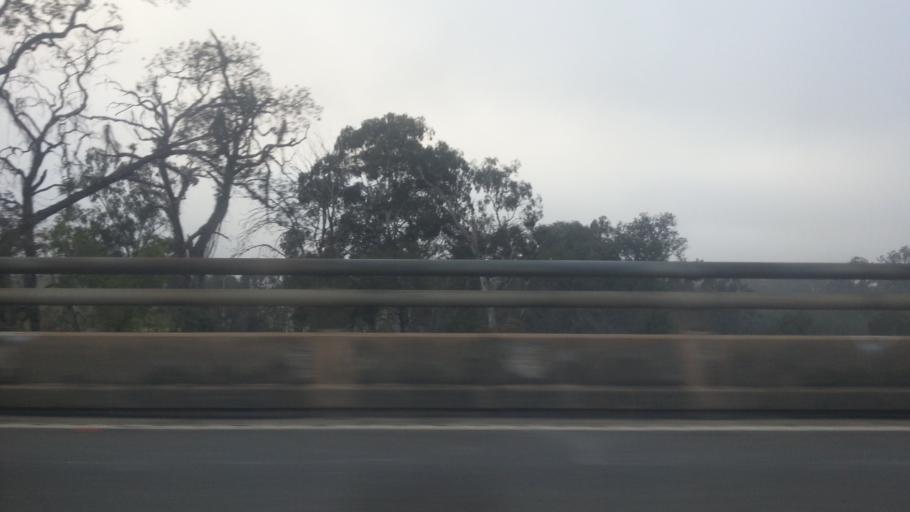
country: AU
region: New South Wales
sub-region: Camden
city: Camden South
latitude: -34.0712
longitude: 150.7002
